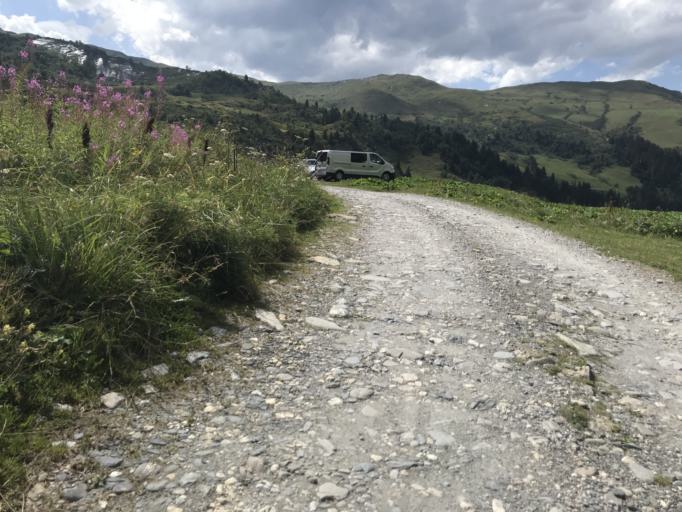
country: FR
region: Rhone-Alpes
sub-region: Departement de la Savoie
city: Beaufort
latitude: 45.6617
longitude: 6.6283
